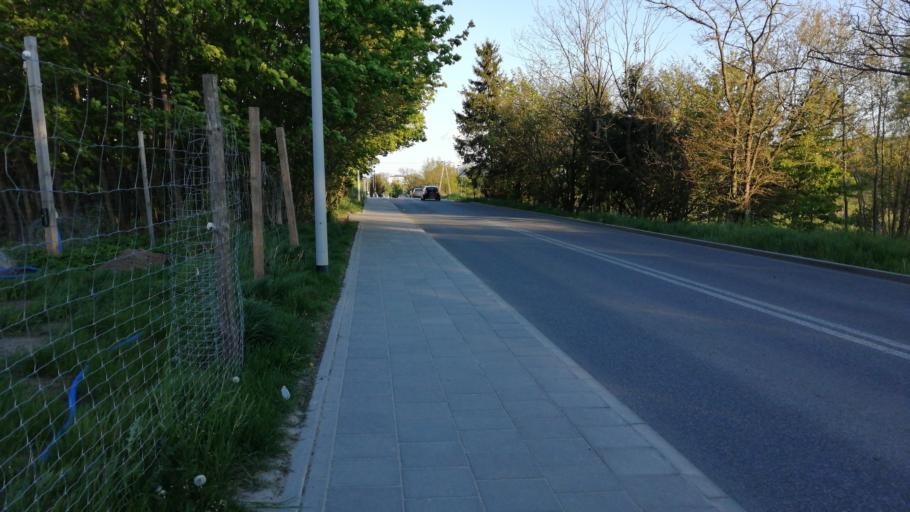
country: PL
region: Pomeranian Voivodeship
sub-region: Powiat gdanski
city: Kowale
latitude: 54.3145
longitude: 18.5947
